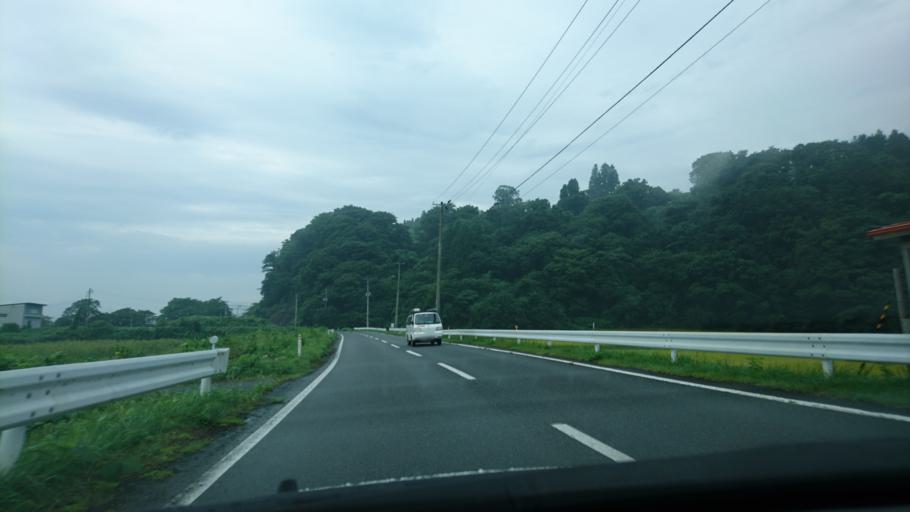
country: JP
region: Iwate
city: Ichinoseki
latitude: 38.8886
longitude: 141.2664
